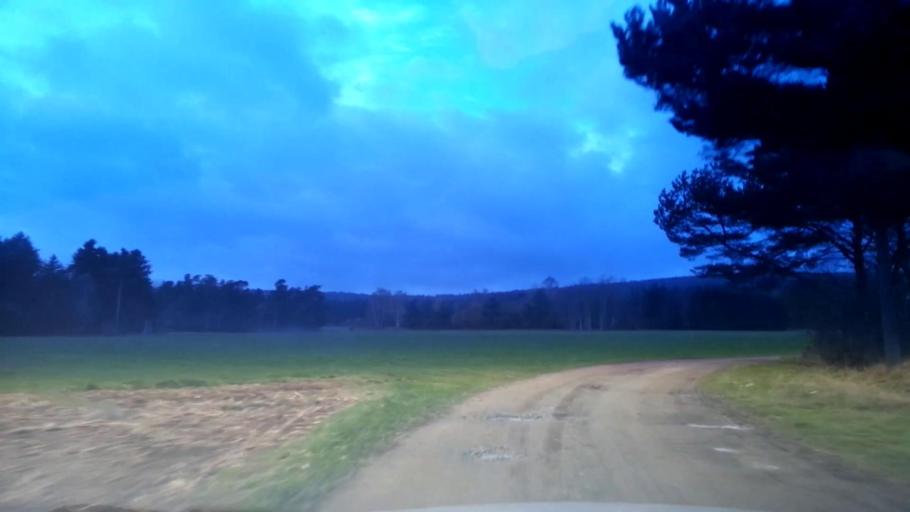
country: DE
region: Bavaria
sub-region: Upper Palatinate
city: Pechbrunn
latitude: 49.9416
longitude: 12.1796
